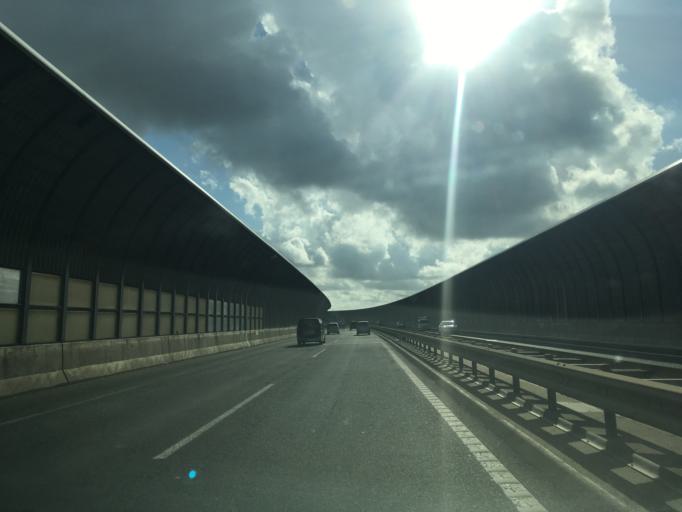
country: JP
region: Saitama
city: Koshigaya
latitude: 35.8479
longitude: 139.7818
